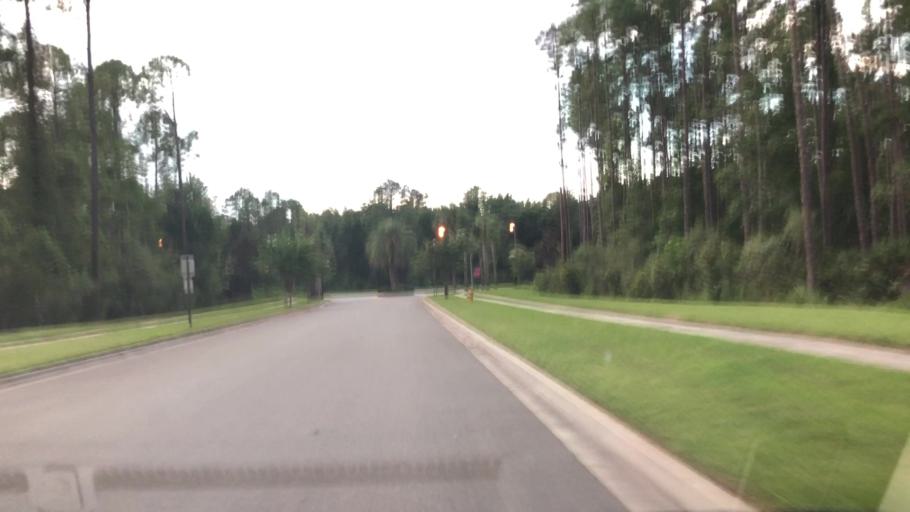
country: US
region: Florida
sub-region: Saint Johns County
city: Palm Valley
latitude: 30.1207
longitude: -81.4457
